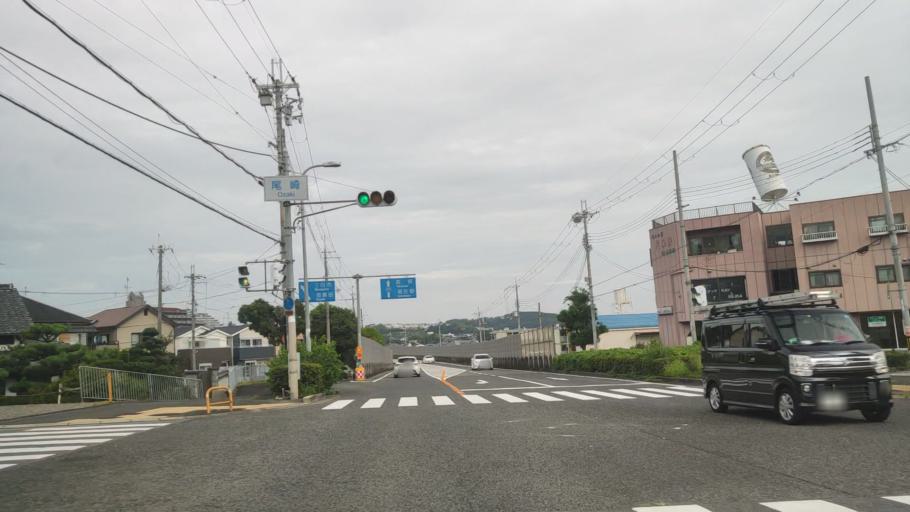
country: JP
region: Osaka
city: Tondabayashicho
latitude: 34.4287
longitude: 135.5698
